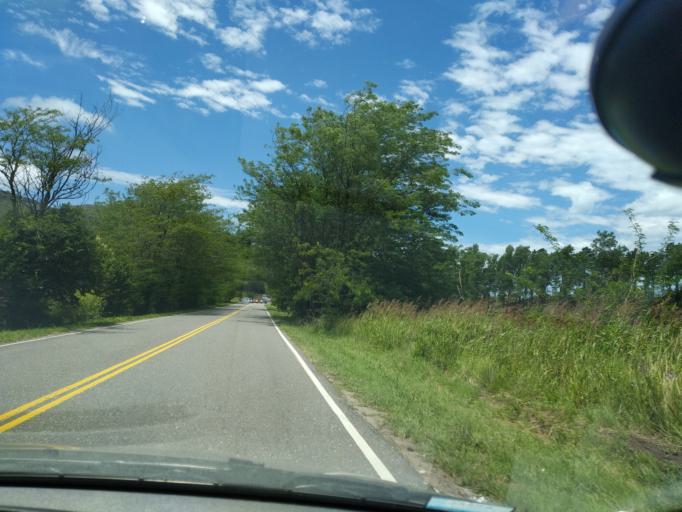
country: AR
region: Cordoba
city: Cuesta Blanca
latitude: -31.6042
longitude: -64.5626
